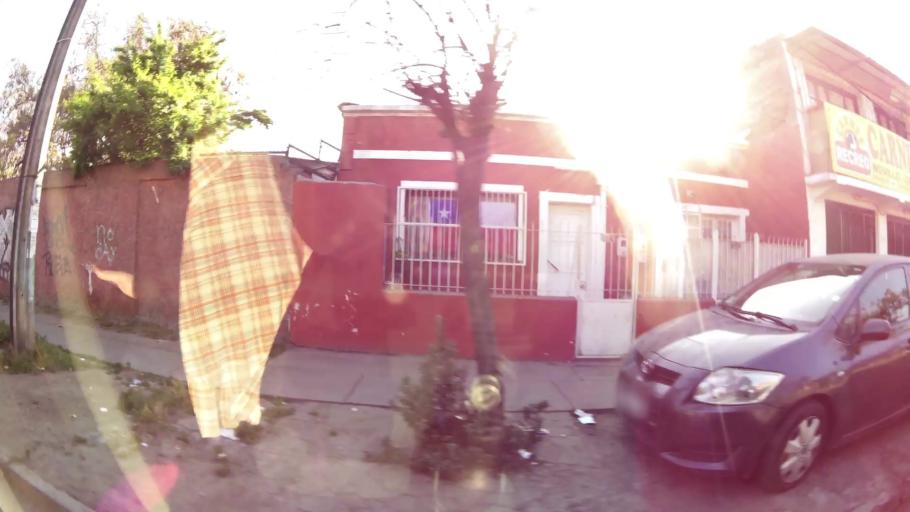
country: CL
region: Santiago Metropolitan
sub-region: Provincia de Santiago
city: Santiago
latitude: -33.3788
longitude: -70.6719
